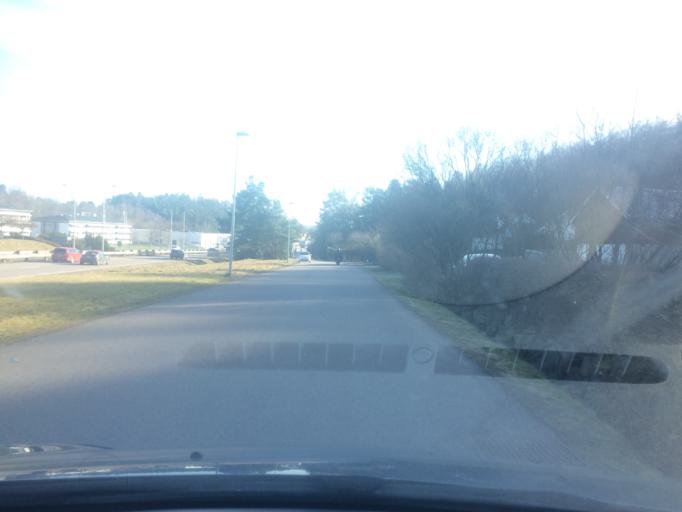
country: SE
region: Vaestra Goetaland
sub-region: Goteborg
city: Goeteborg
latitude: 57.7404
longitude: 11.9403
